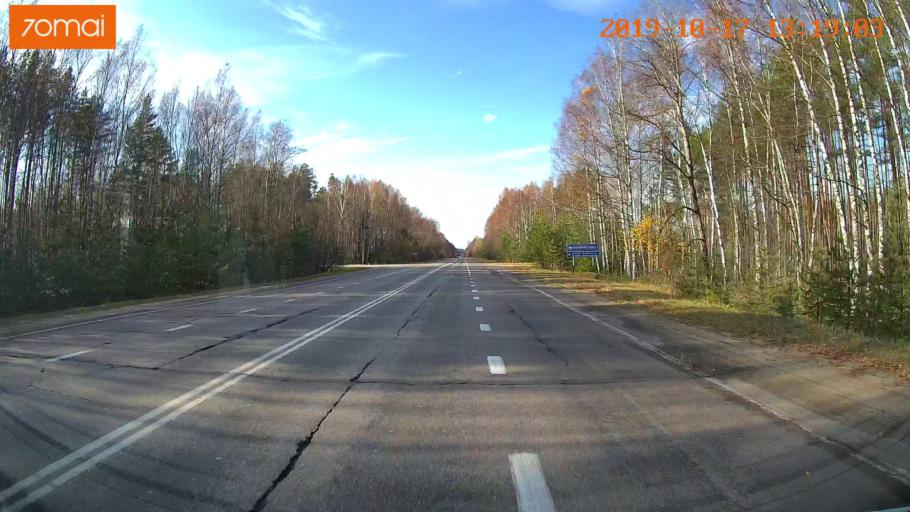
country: RU
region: Rjazan
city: Gus'-Zheleznyy
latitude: 55.0669
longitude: 41.0833
